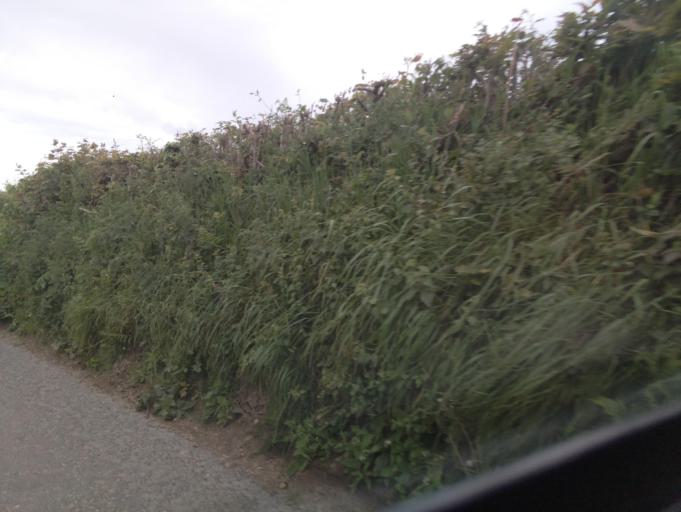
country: GB
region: England
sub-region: Devon
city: Dartmouth
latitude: 50.3266
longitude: -3.6412
